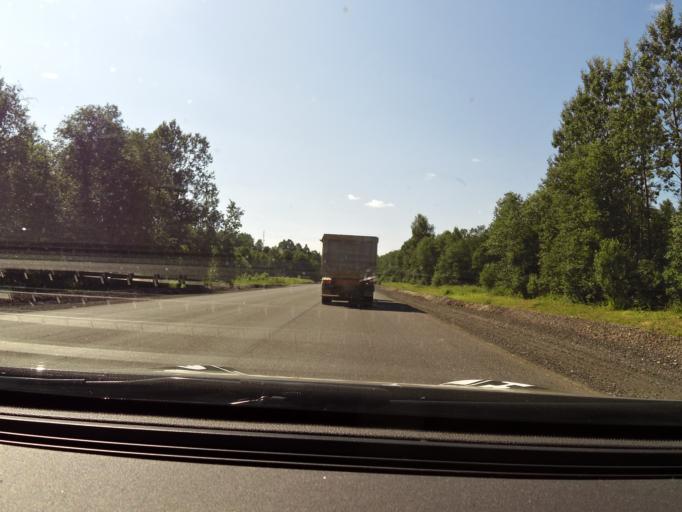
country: RU
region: Novgorod
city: Proletariy
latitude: 58.3672
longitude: 32.1085
